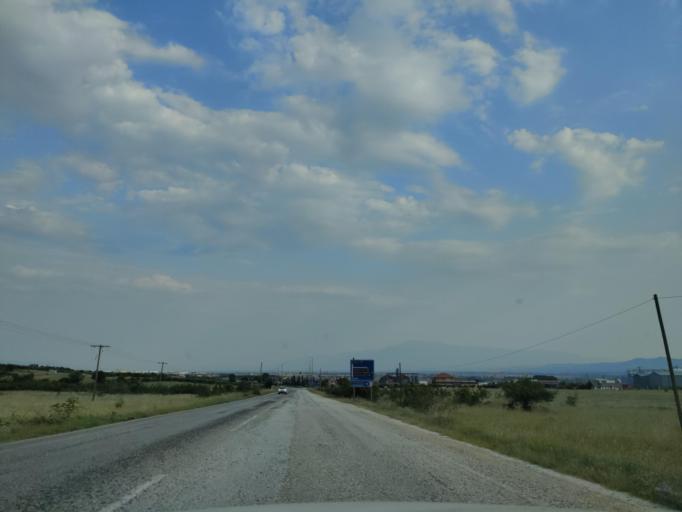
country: GR
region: East Macedonia and Thrace
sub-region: Nomos Dramas
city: Prosotsani
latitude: 41.1979
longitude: 23.9625
